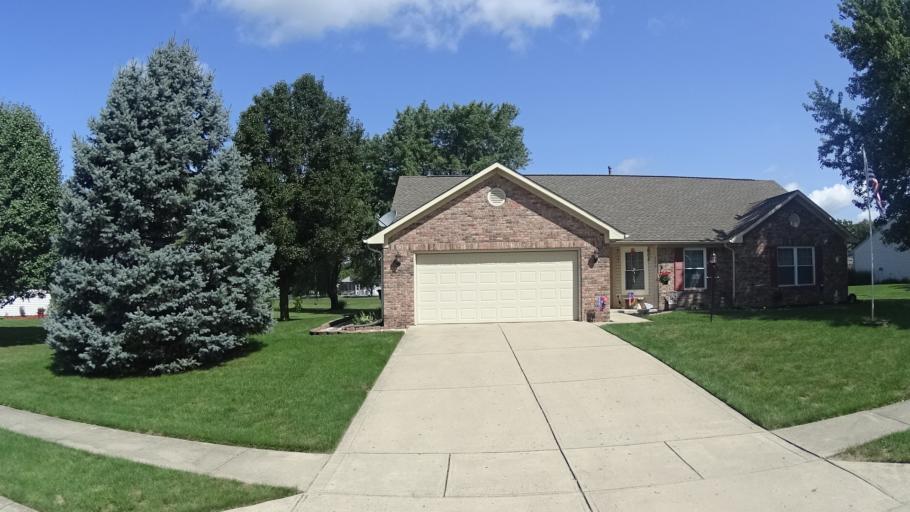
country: US
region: Indiana
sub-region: Madison County
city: Pendleton
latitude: 39.9875
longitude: -85.7463
